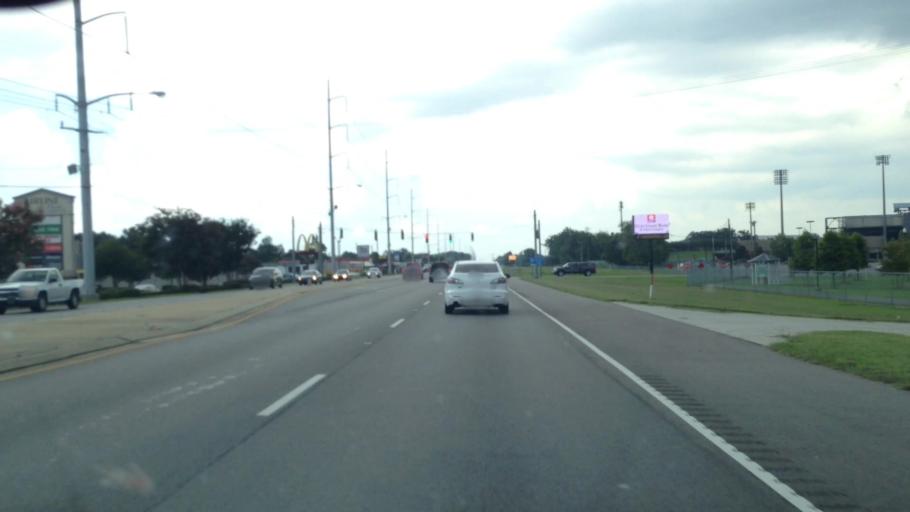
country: US
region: Louisiana
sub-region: Jefferson Parish
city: River Ridge
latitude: 29.9773
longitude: -90.2043
